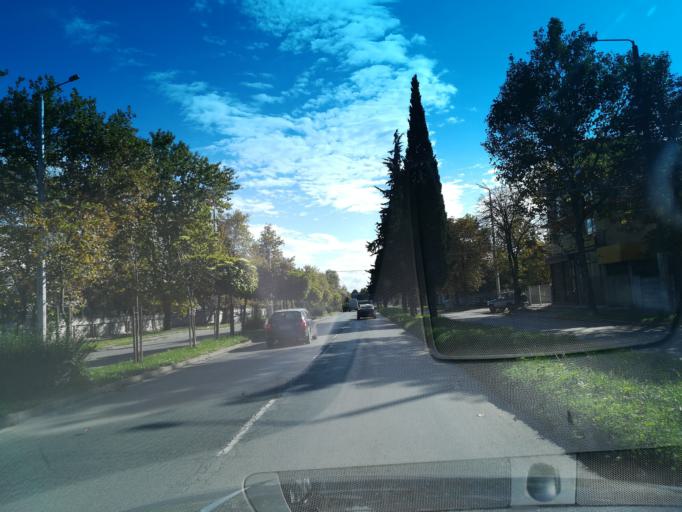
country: BG
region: Stara Zagora
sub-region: Obshtina Stara Zagora
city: Stara Zagora
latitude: 42.4120
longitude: 25.6390
